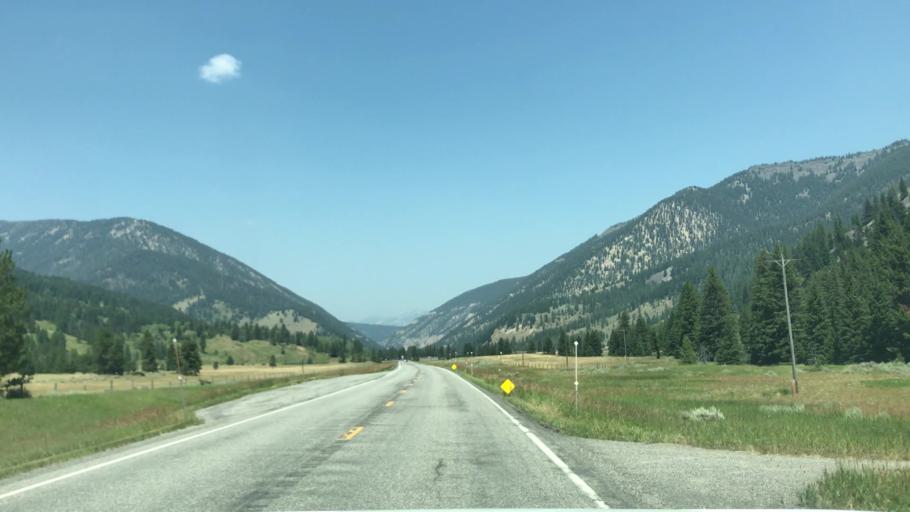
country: US
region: Montana
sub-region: Gallatin County
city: Big Sky
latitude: 45.0930
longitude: -111.2144
